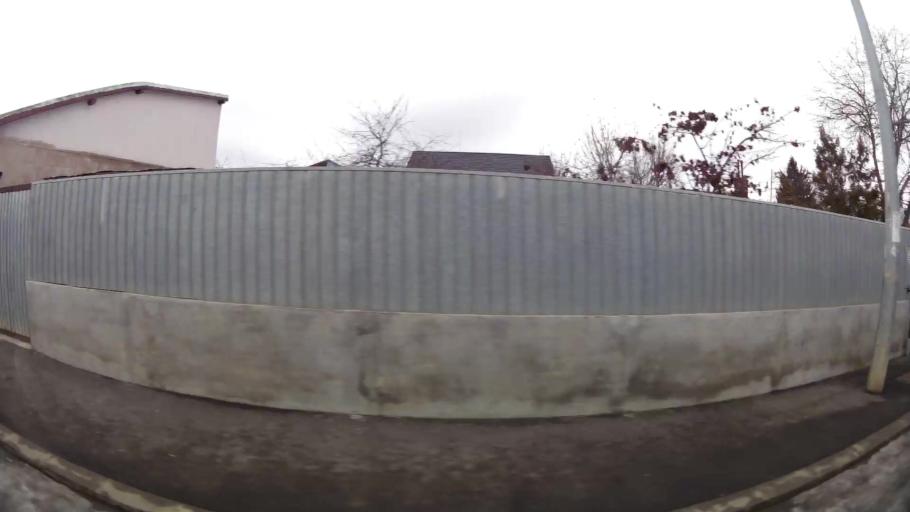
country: RO
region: Ilfov
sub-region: Comuna Pantelimon
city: Pantelimon
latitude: 44.4491
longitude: 26.1994
